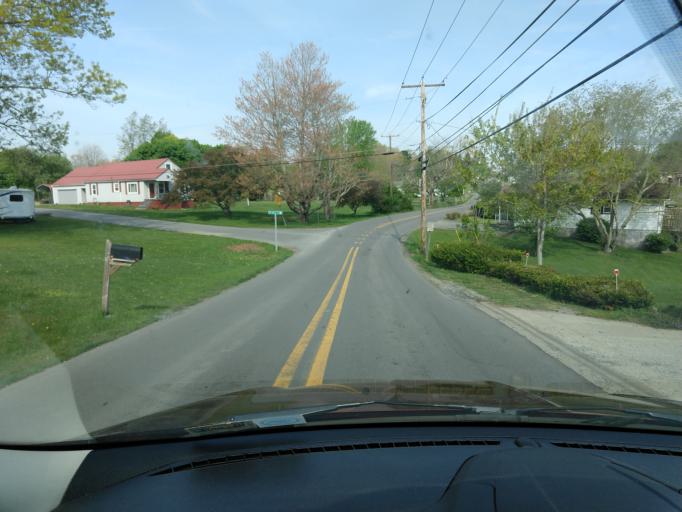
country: US
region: West Virginia
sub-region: Raleigh County
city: Crab Orchard
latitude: 37.7470
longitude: -81.2344
